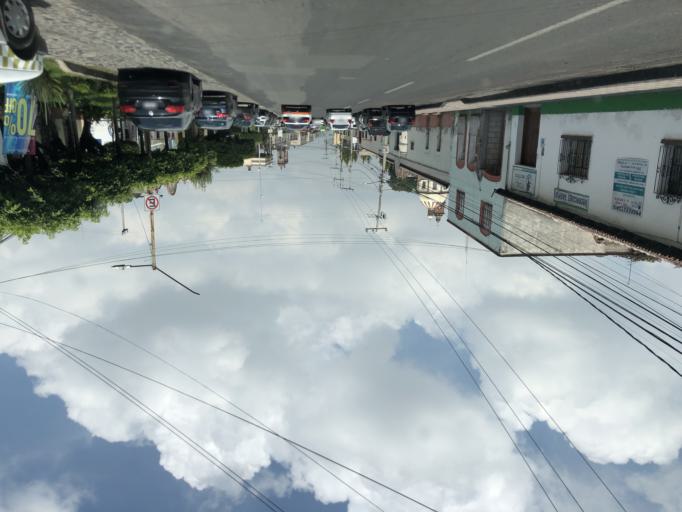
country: MX
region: Morelos
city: Lerma de Villada
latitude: 19.2862
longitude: -99.5087
